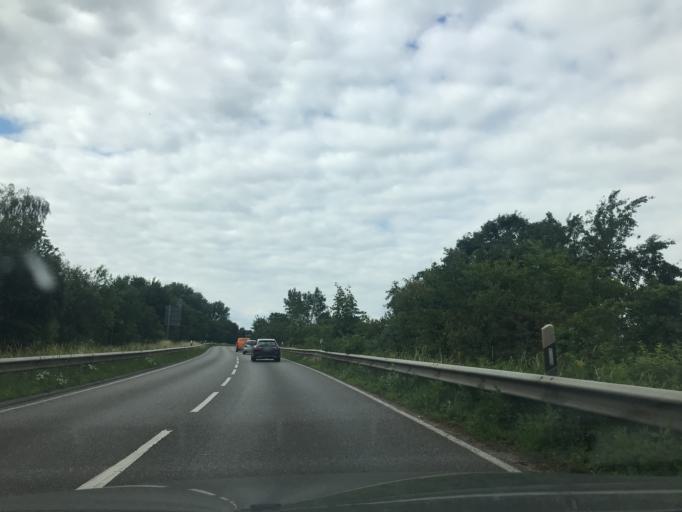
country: DE
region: North Rhine-Westphalia
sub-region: Regierungsbezirk Dusseldorf
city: Neuss
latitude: 51.1623
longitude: 6.7237
